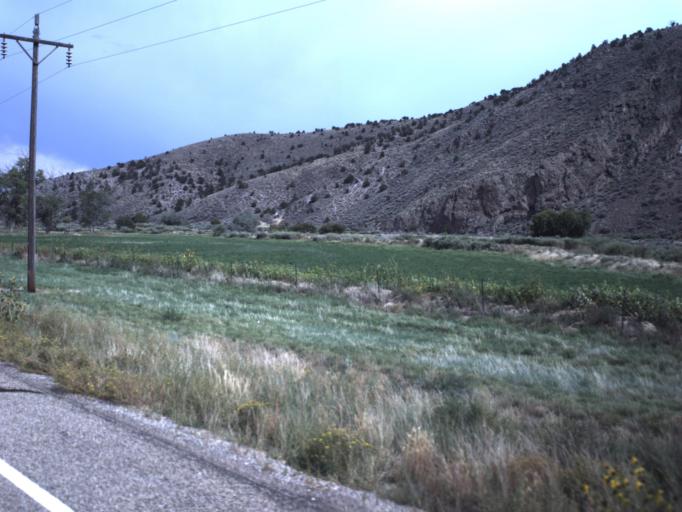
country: US
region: Utah
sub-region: Piute County
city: Junction
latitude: 38.1456
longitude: -112.3009
